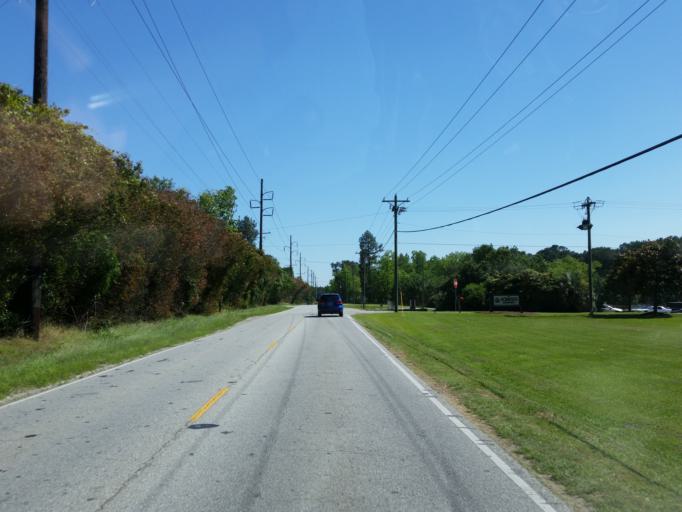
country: US
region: Georgia
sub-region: Lowndes County
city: Hahira
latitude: 30.9320
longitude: -83.3498
